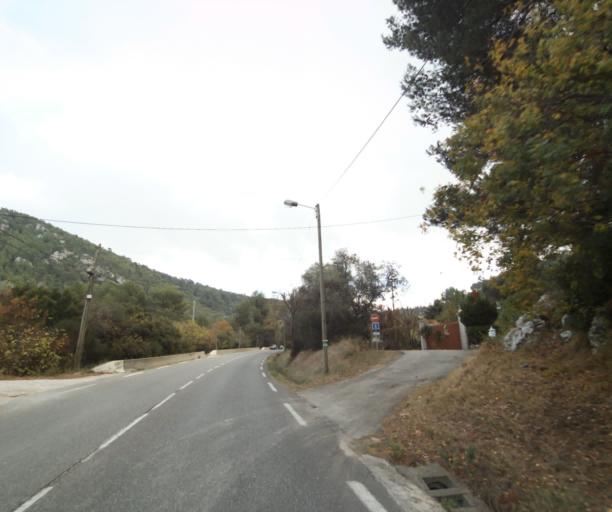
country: FR
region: Provence-Alpes-Cote d'Azur
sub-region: Departement des Bouches-du-Rhone
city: Gemenos
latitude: 43.2722
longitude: 5.6427
